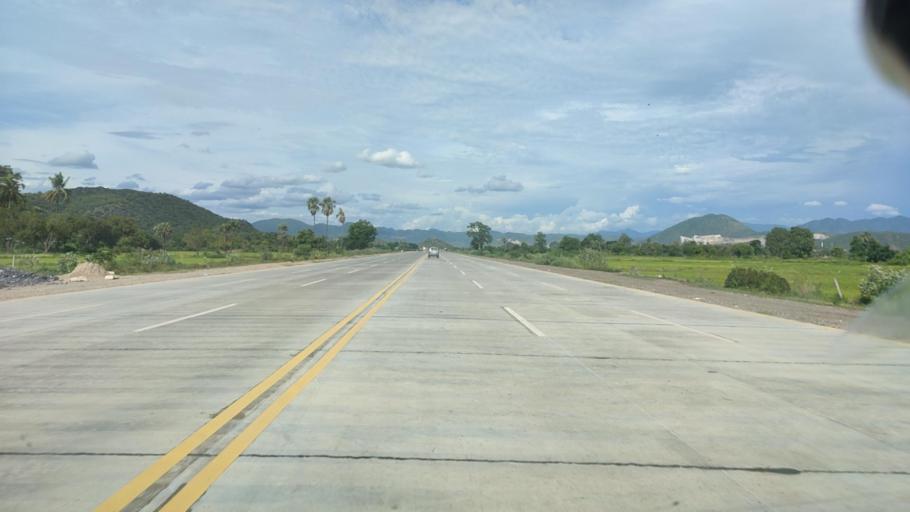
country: MM
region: Mandalay
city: Kyaukse
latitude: 21.5972
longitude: 96.1687
